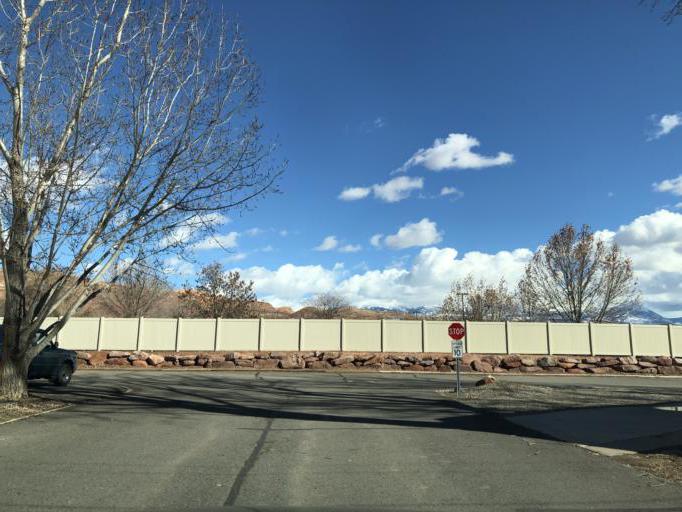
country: US
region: Utah
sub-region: Grand County
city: Moab
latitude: 38.5763
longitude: -109.5618
